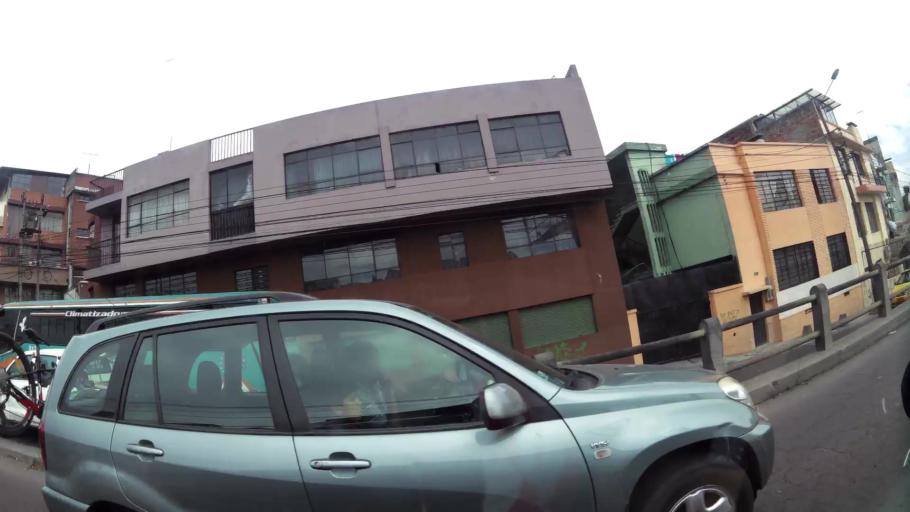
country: EC
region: Pichincha
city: Quito
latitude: -0.2159
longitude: -78.4912
